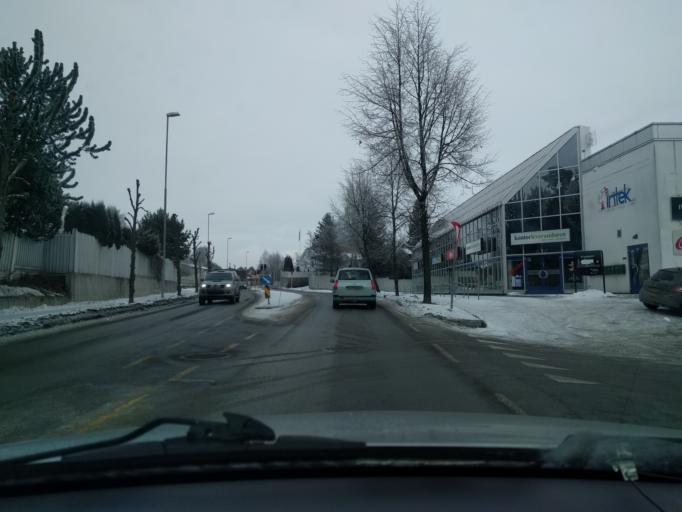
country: NO
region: Hedmark
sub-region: Hamar
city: Hamar
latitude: 60.8024
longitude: 11.0775
